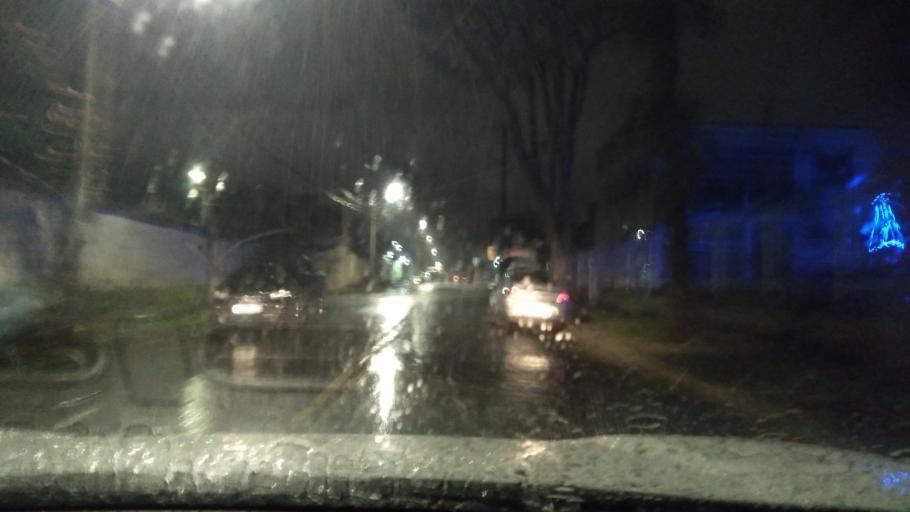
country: BR
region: Minas Gerais
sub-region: Belo Horizonte
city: Belo Horizonte
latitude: -19.8795
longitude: -43.9402
